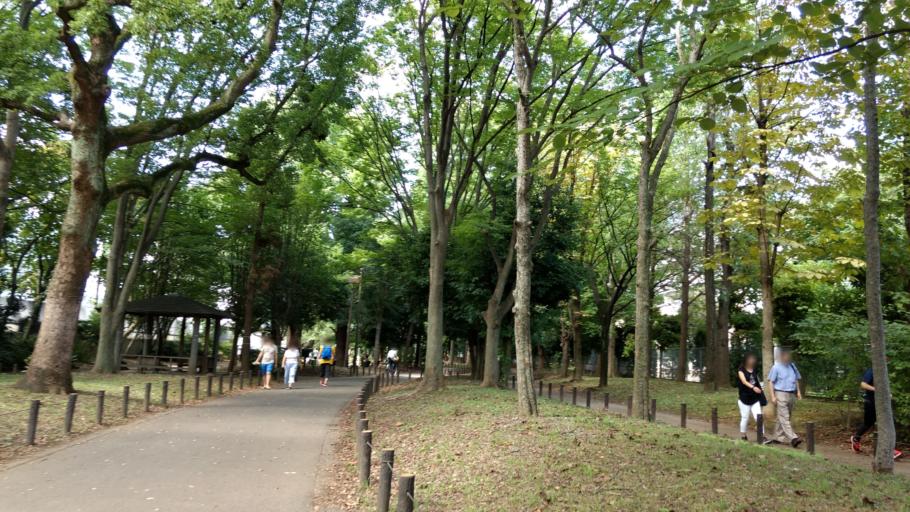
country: JP
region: Tokyo
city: Tokyo
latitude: 35.7069
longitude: 139.7079
